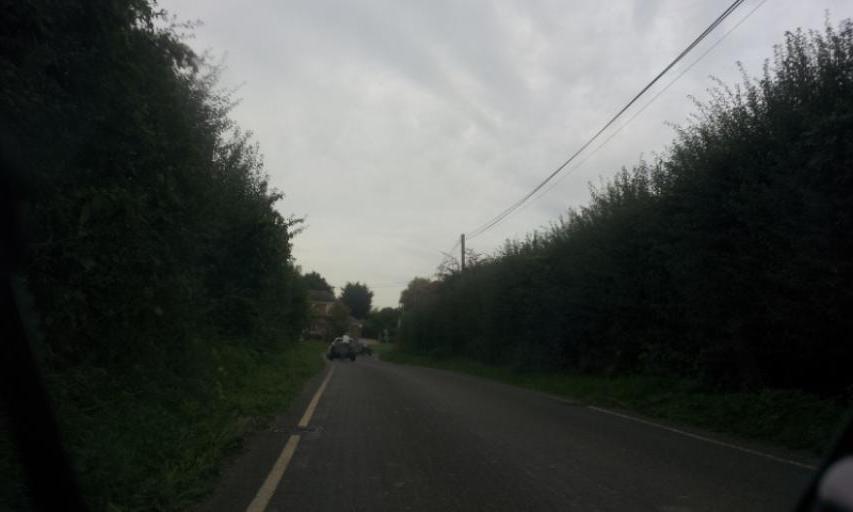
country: GB
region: England
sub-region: Kent
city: Hadlow
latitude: 51.2093
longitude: 0.3411
